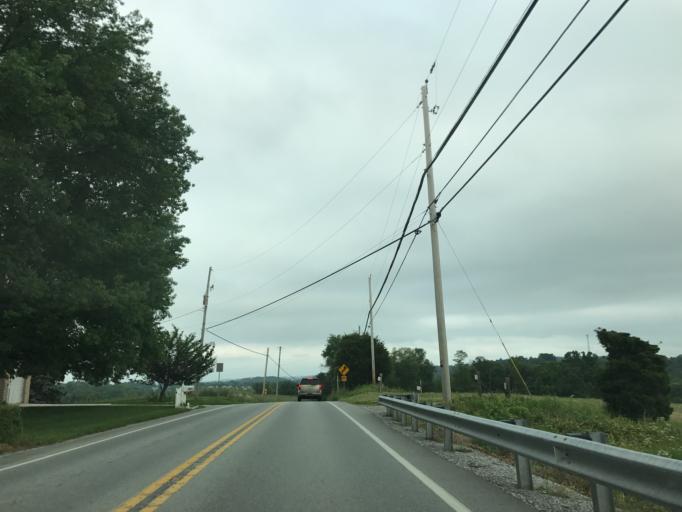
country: US
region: Pennsylvania
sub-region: York County
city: Wrightsville
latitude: 39.9662
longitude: -76.5437
